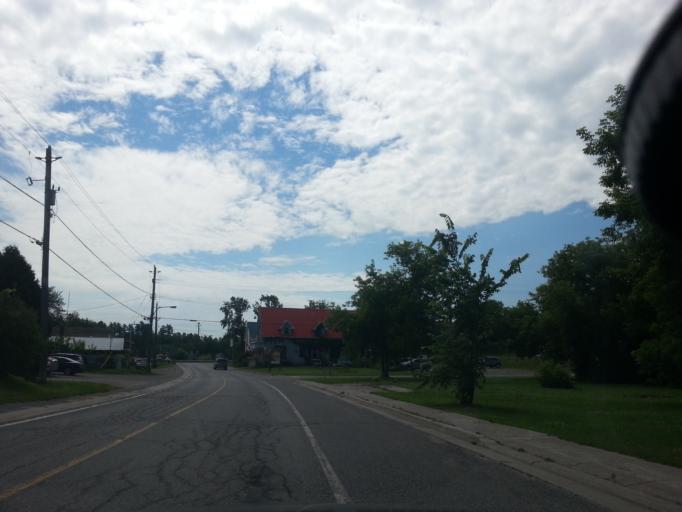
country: CA
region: Ontario
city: Renfrew
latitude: 45.3003
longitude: -76.7224
